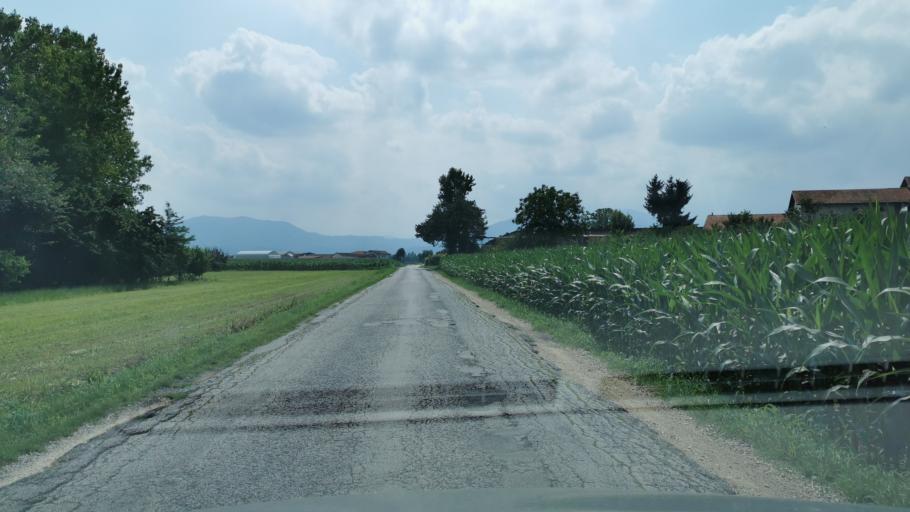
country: IT
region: Piedmont
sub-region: Provincia di Cuneo
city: Roata Rossi
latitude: 44.4334
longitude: 7.4918
